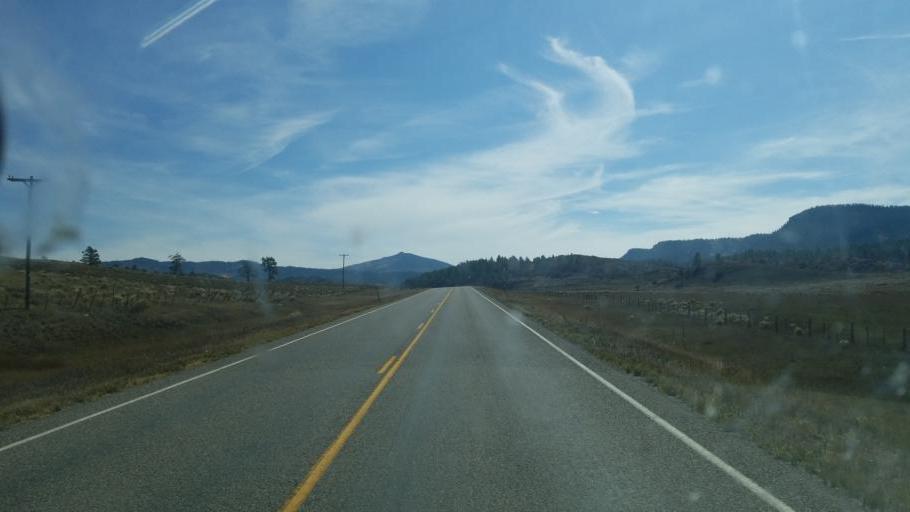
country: US
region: New Mexico
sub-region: Rio Arriba County
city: Dulce
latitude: 37.0247
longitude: -106.8214
